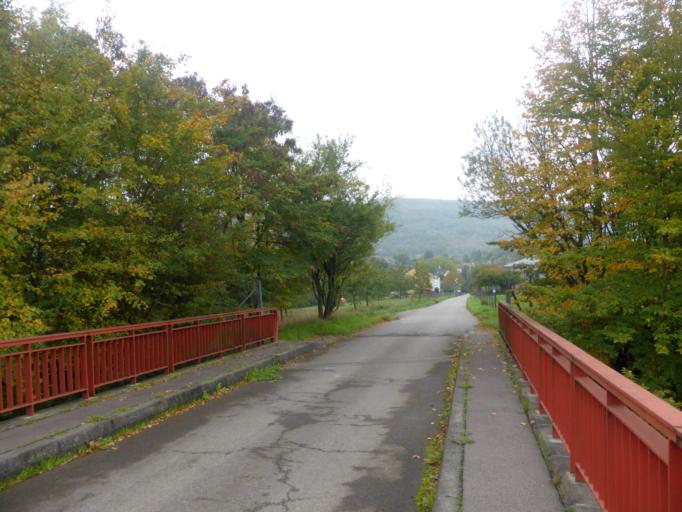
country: LU
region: Grevenmacher
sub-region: Canton de Grevenmacher
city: Mertert
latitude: 49.7074
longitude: 6.4767
